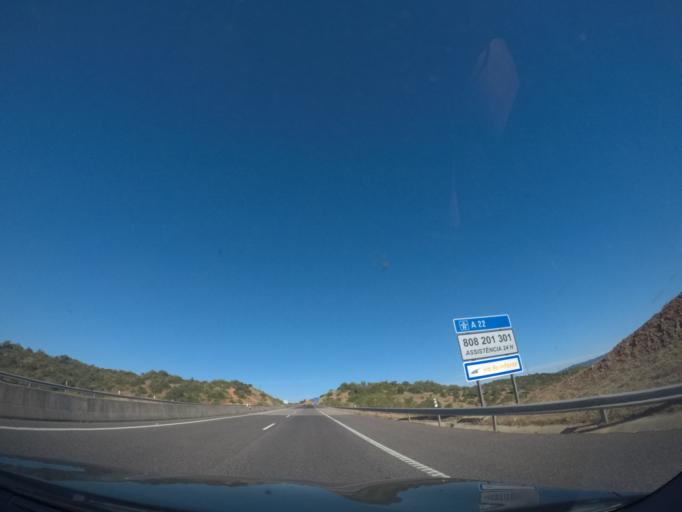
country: PT
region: Faro
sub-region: Portimao
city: Portimao
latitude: 37.1776
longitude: -8.5475
